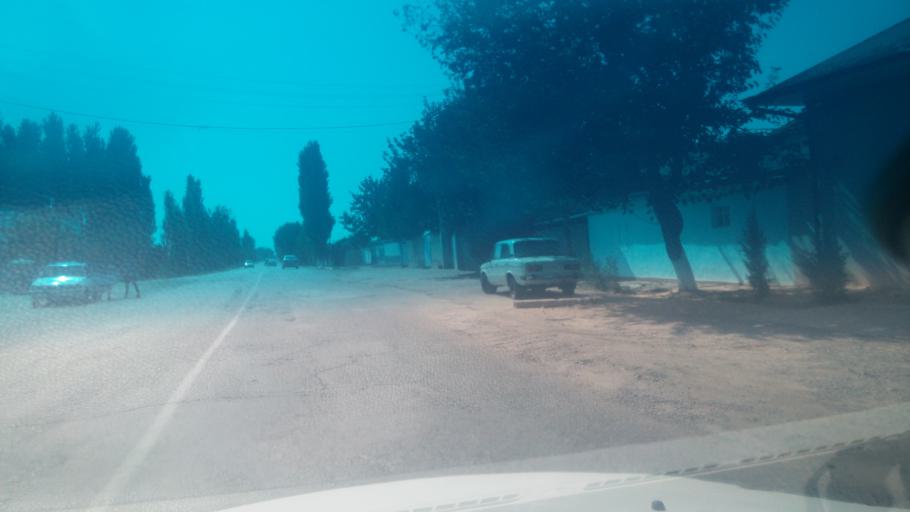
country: UZ
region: Sirdaryo
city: Sirdaryo
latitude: 40.8198
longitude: 68.6739
